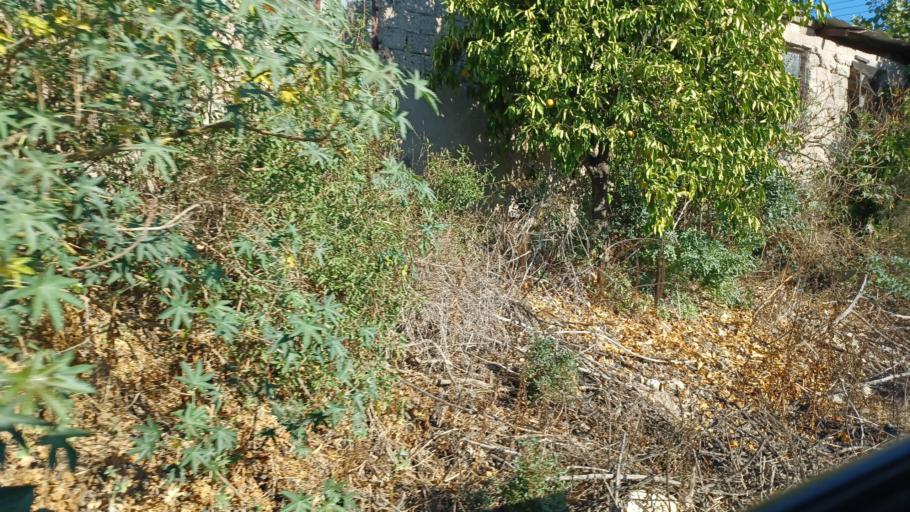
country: CY
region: Pafos
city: Mesogi
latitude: 34.8767
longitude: 32.5041
